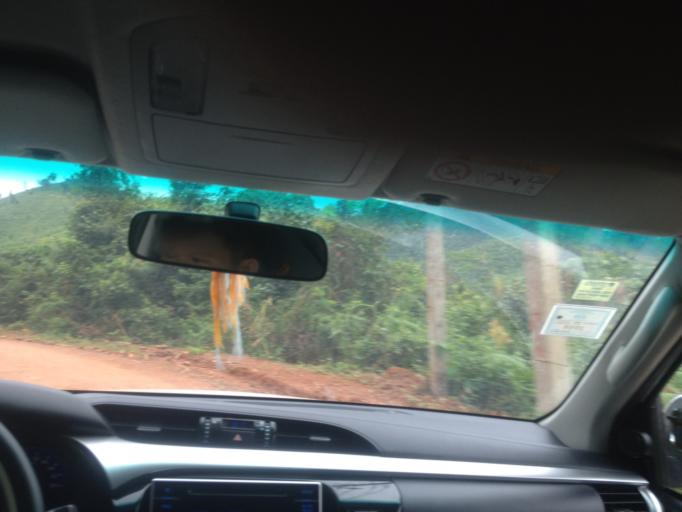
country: TH
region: Nan
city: Chaloem Phra Kiat
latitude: 19.9667
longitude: 101.1386
